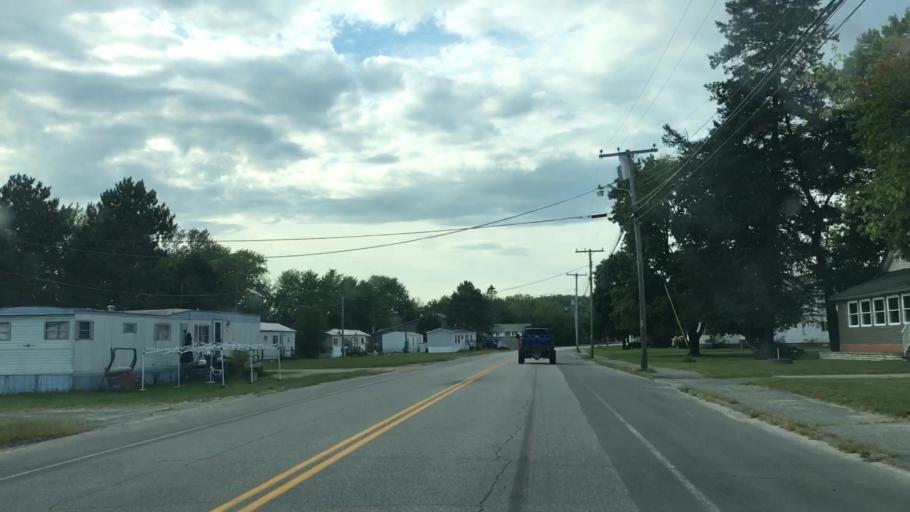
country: US
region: Maine
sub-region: Penobscot County
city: Howland
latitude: 45.2426
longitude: -68.6600
